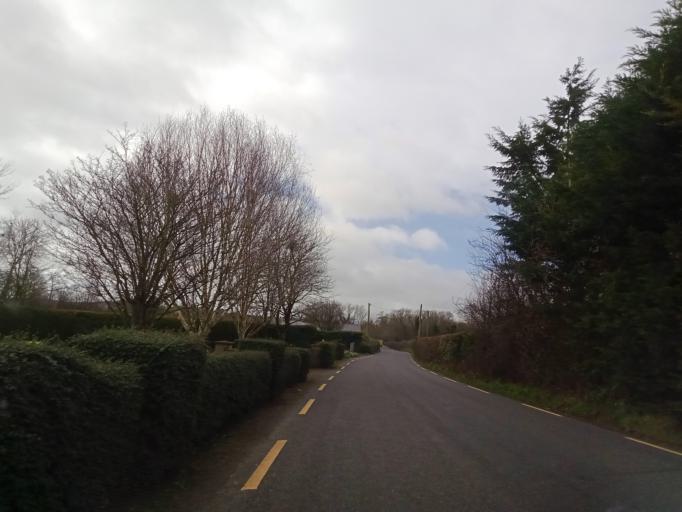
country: IE
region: Leinster
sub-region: Kilkenny
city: Ballyragget
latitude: 52.7192
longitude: -7.3154
